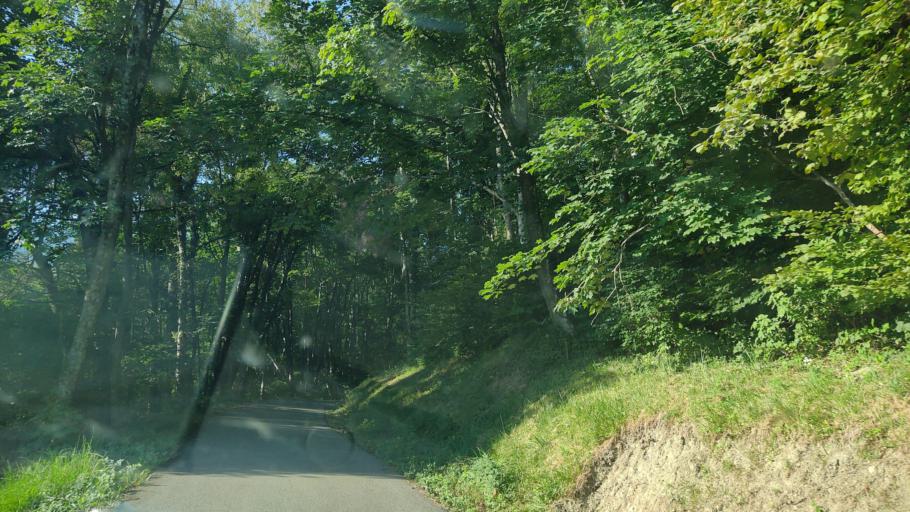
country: FR
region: Rhone-Alpes
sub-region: Departement de la Savoie
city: Saint-Etienne-de-Cuines
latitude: 45.3415
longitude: 6.2777
